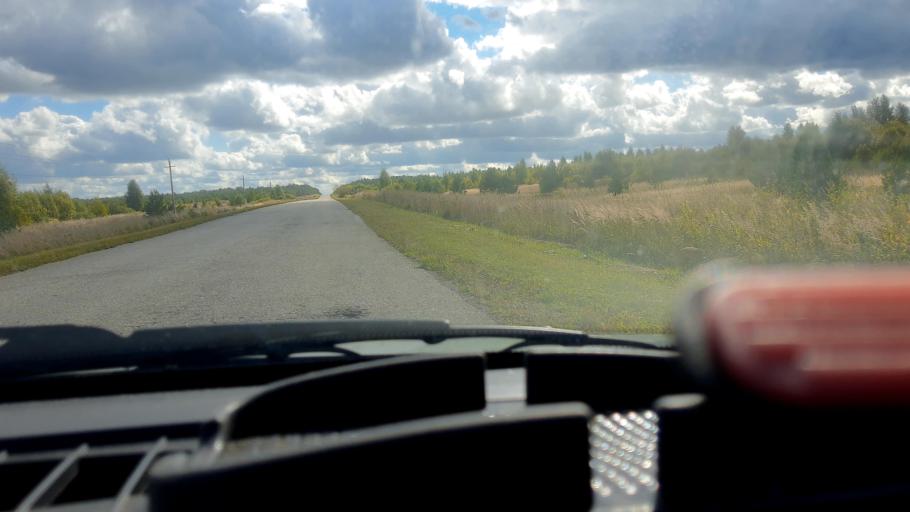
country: RU
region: Mariy-El
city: Kilemary
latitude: 56.9385
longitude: 46.6913
